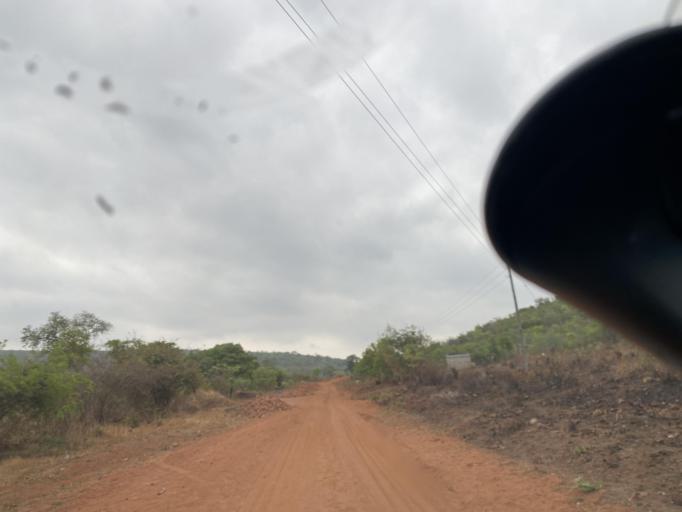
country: ZM
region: Lusaka
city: Chongwe
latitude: -15.1817
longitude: 28.7632
